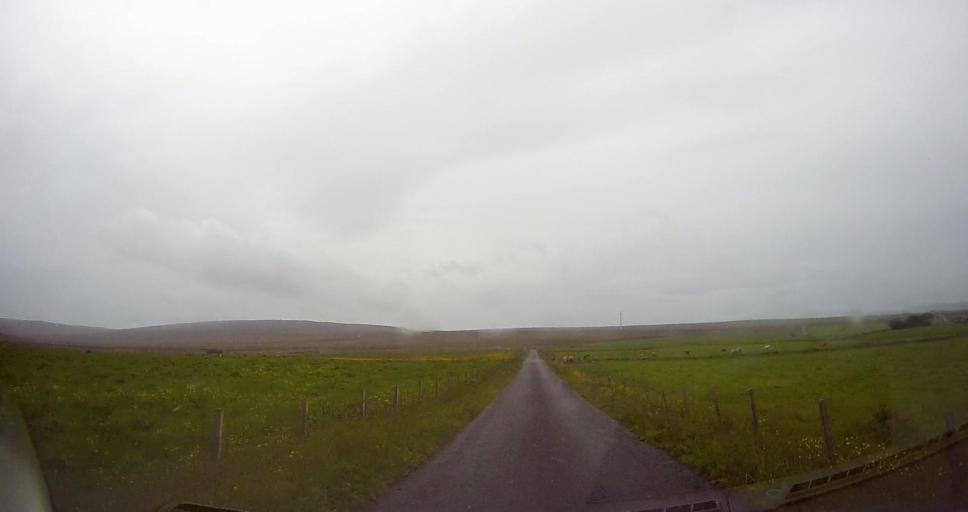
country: GB
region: Scotland
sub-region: Orkney Islands
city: Stromness
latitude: 59.0915
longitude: -3.1827
